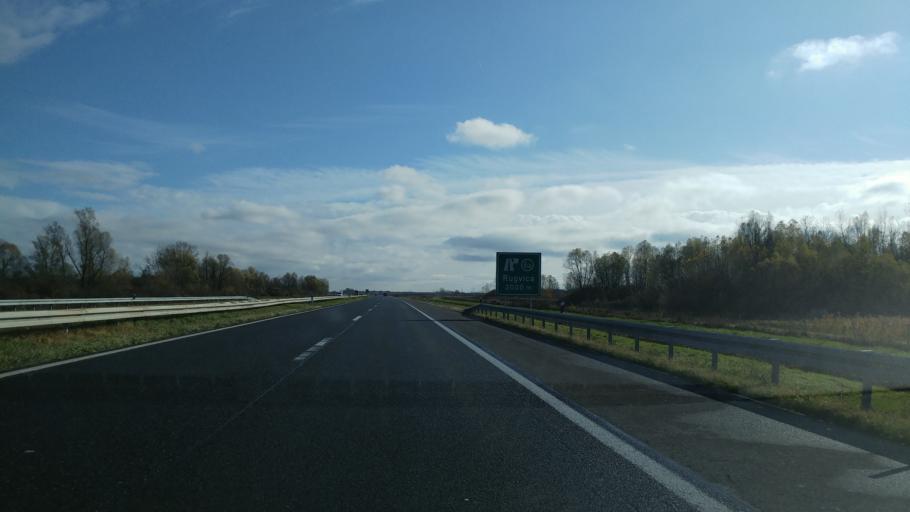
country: HR
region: Grad Zagreb
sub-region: Sesvete
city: Sesvete
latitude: 45.7767
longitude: 16.1989
